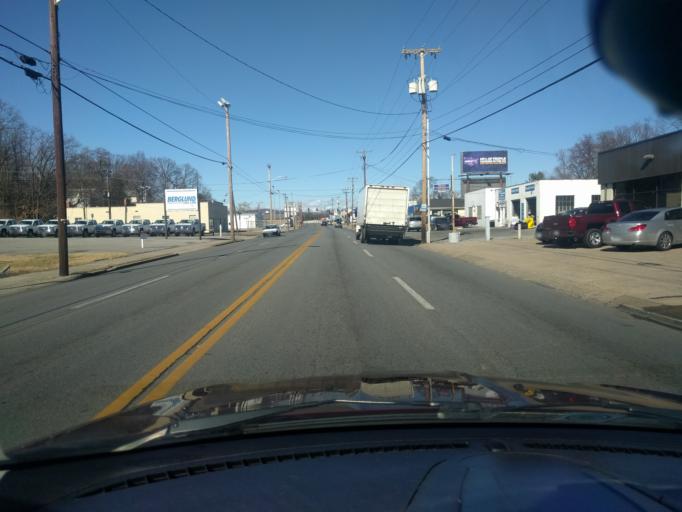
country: US
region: Virginia
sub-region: City of Roanoke
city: Roanoke
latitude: 37.2905
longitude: -79.9345
